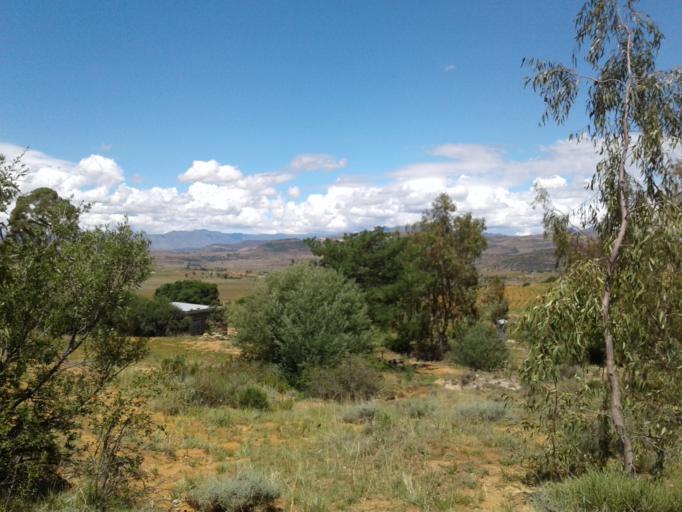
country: LS
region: Quthing
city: Quthing
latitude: -30.3793
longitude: 27.5569
